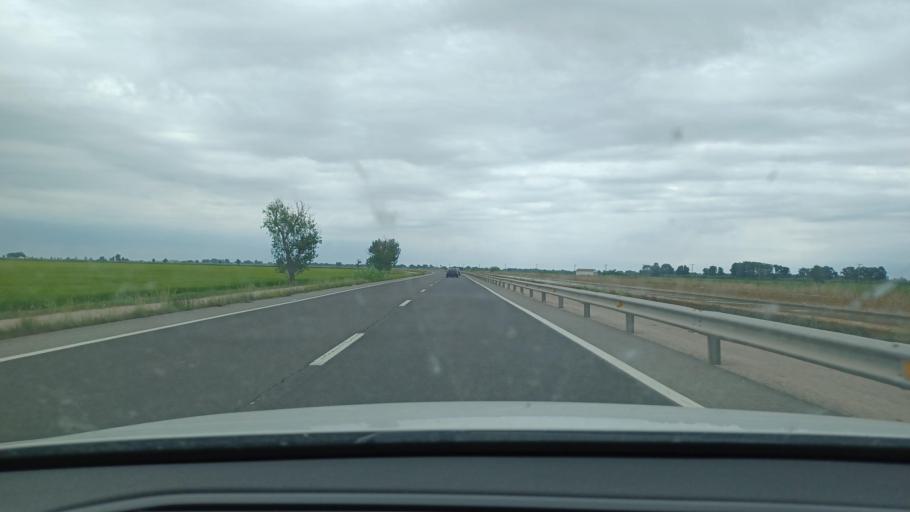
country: ES
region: Catalonia
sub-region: Provincia de Tarragona
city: Amposta
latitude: 40.7124
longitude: 0.6075
